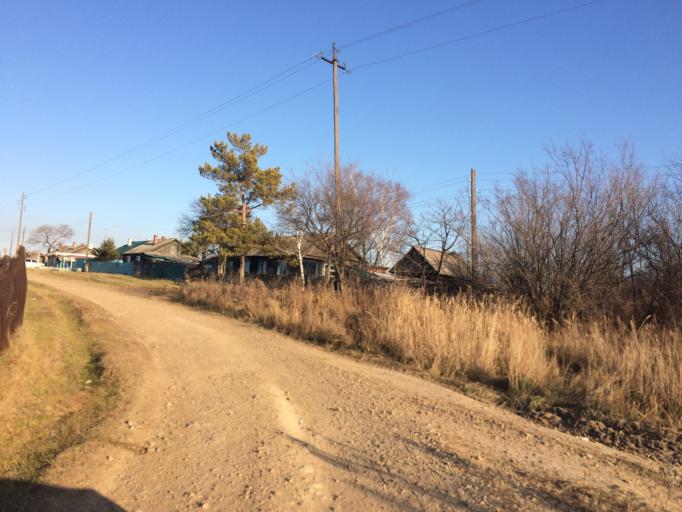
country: RU
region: Primorskiy
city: Ivanovka
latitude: 43.9550
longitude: 132.4686
